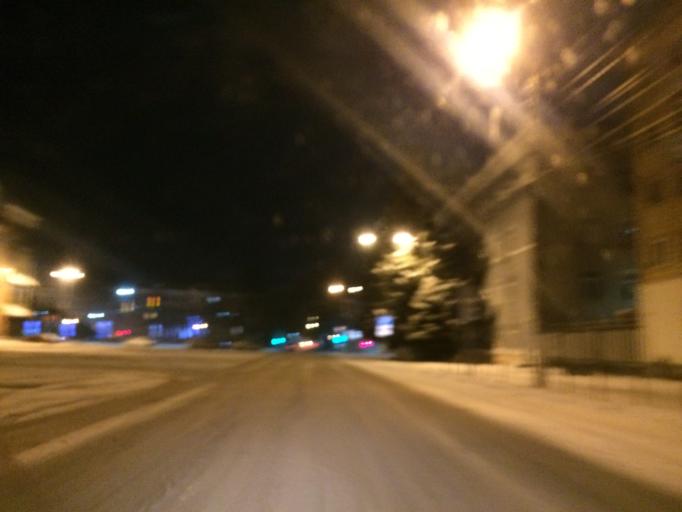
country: RU
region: Tula
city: Tula
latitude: 54.1773
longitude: 37.6024
